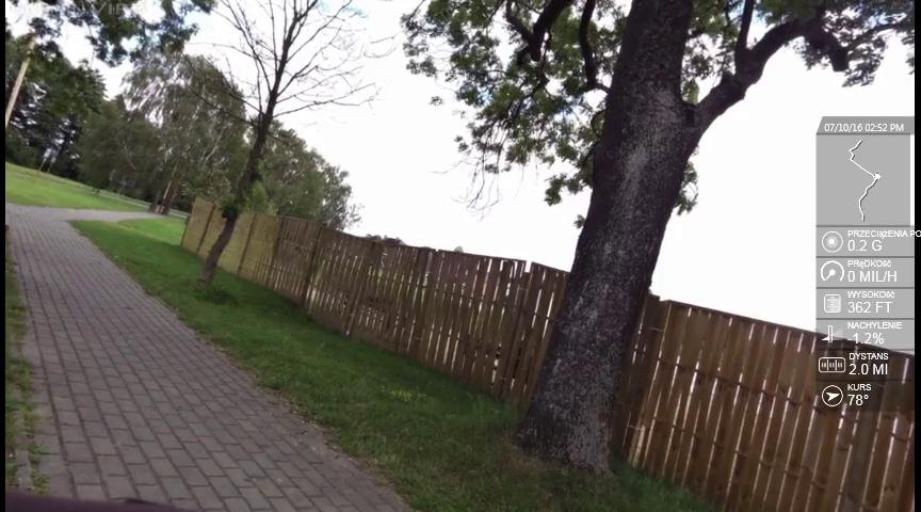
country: PL
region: West Pomeranian Voivodeship
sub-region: Powiat gryfinski
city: Banie
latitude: 53.1013
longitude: 14.6533
